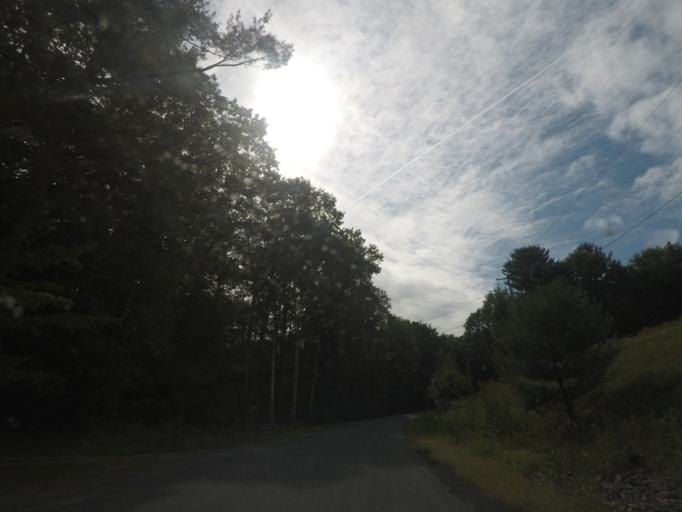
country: US
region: New York
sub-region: Rensselaer County
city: Nassau
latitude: 42.5649
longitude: -73.6172
